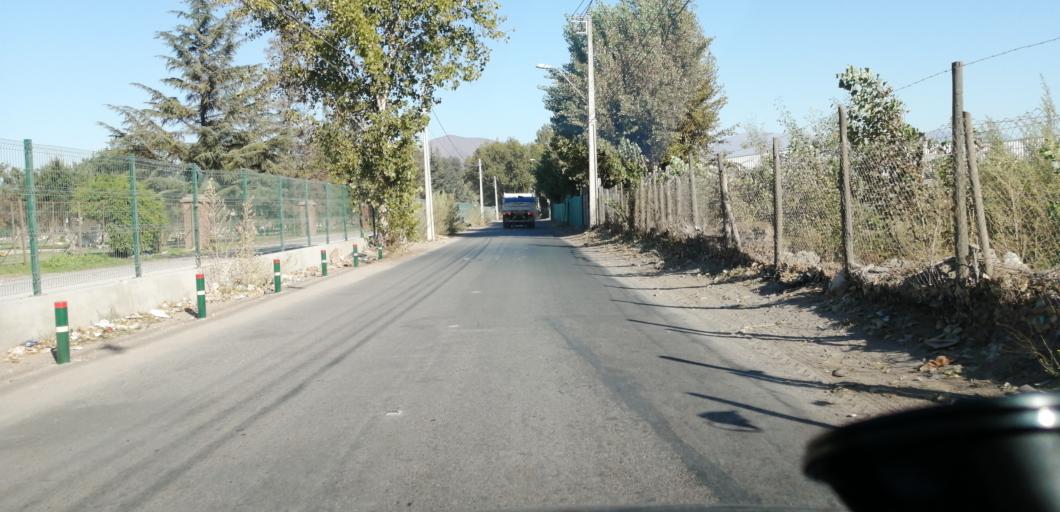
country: CL
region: Santiago Metropolitan
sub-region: Provincia de Santiago
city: Lo Prado
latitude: -33.4633
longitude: -70.7685
